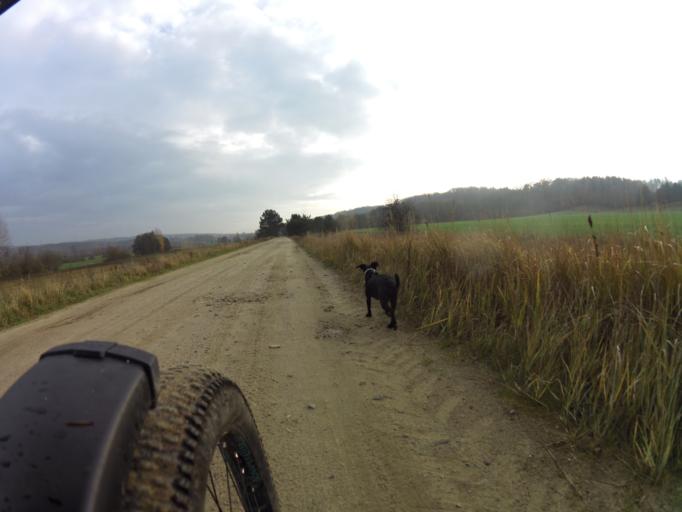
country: PL
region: Pomeranian Voivodeship
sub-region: Powiat wejherowski
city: Gniewino
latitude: 54.7066
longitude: 18.1023
